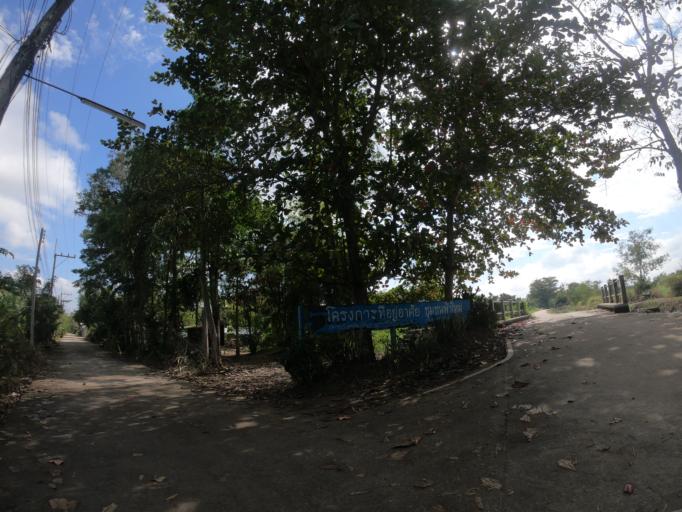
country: TH
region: Chiang Mai
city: Hang Dong
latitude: 18.6955
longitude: 98.9768
